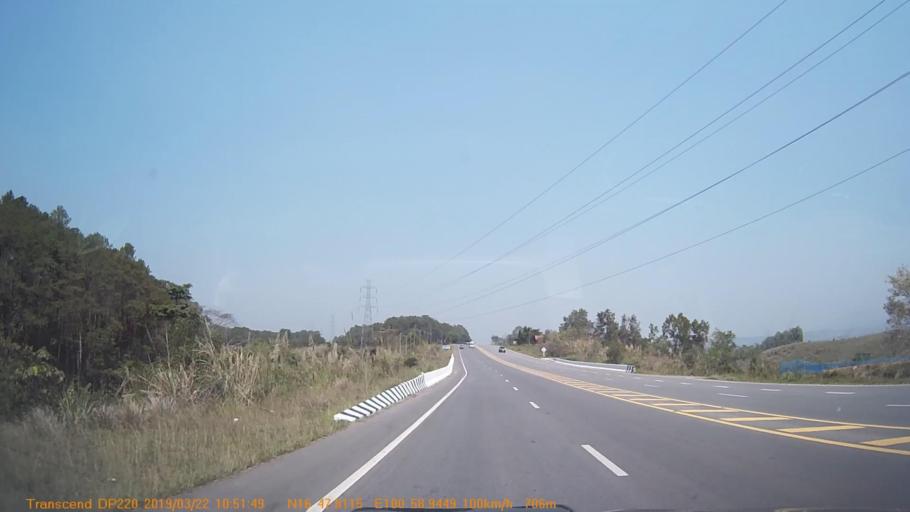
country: TH
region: Phetchabun
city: Khao Kho
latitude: 16.7972
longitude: 100.9822
